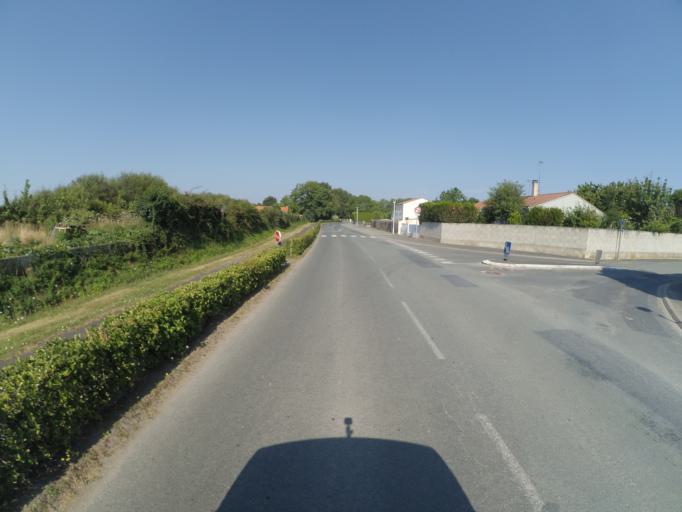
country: FR
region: Pays de la Loire
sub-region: Departement de la Vendee
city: Treize-Septiers
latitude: 46.9865
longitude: -1.2232
